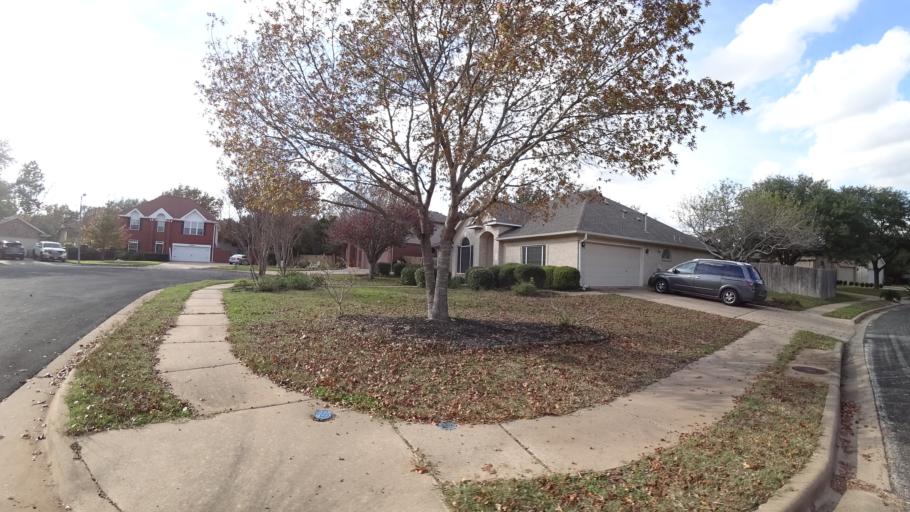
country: US
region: Texas
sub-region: Williamson County
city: Brushy Creek
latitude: 30.5087
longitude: -97.7324
